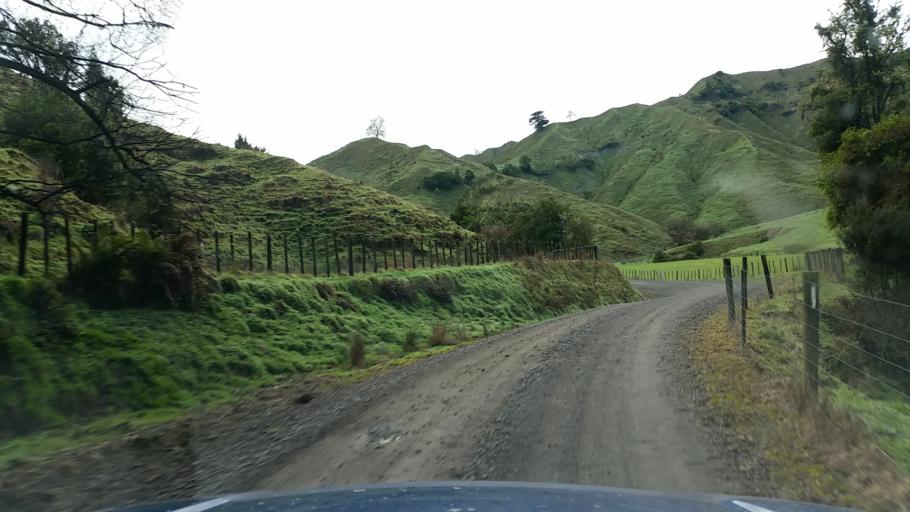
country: NZ
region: Taranaki
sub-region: New Plymouth District
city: Waitara
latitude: -39.0953
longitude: 174.8386
